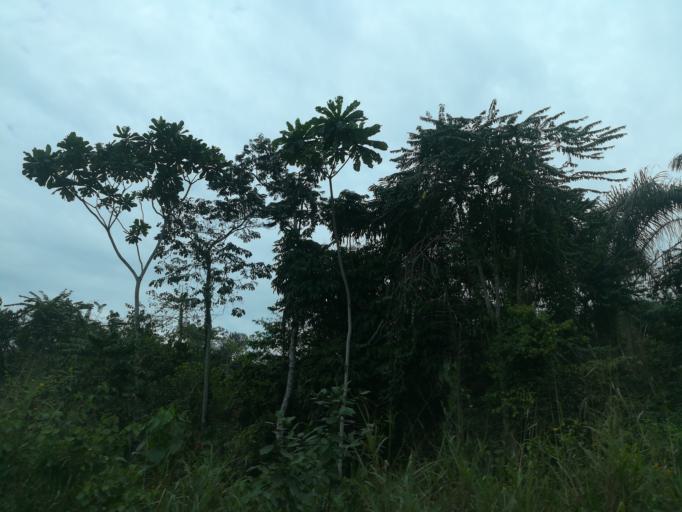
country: NG
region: Lagos
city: Ejirin
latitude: 6.6620
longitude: 3.8139
